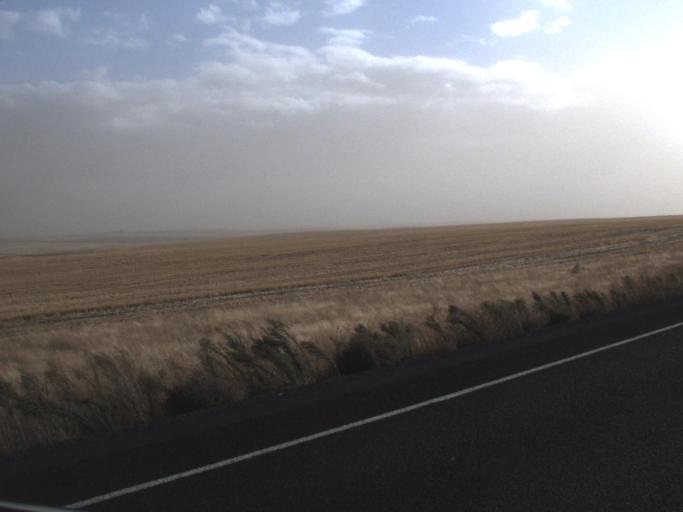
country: US
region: Washington
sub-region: Lincoln County
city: Davenport
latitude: 47.4482
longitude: -118.3180
